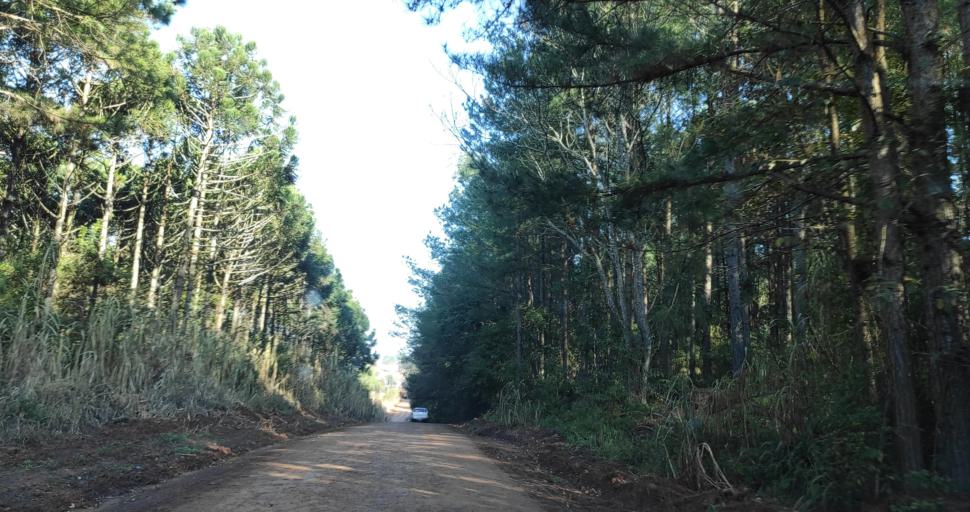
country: AR
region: Misiones
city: Puerto Rico
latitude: -26.8645
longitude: -55.0368
